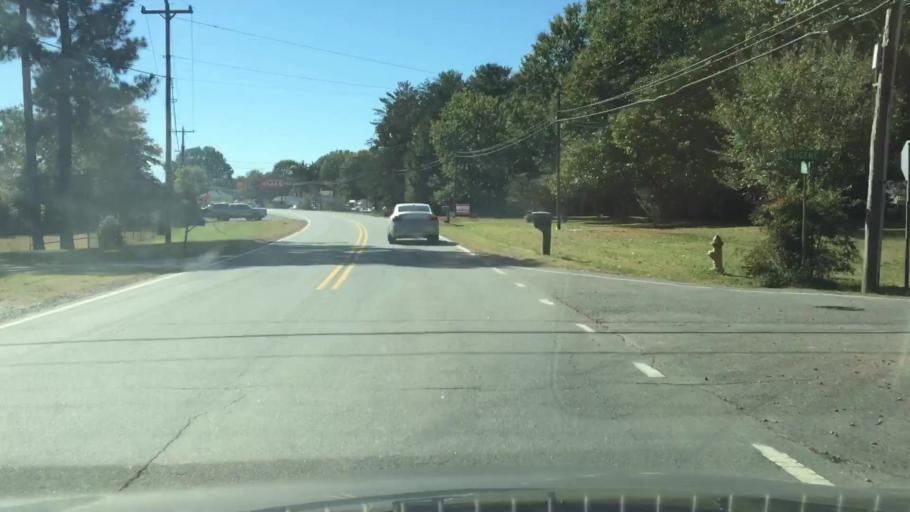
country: US
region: North Carolina
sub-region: Rockingham County
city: Reidsville
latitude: 36.3223
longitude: -79.6709
